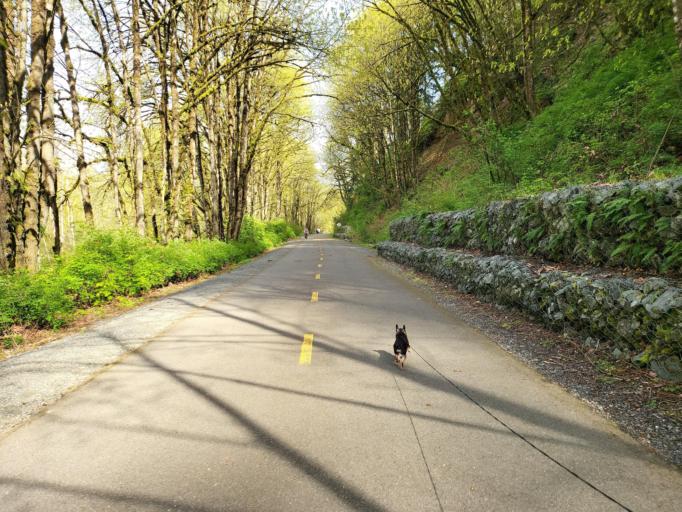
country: US
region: Washington
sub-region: King County
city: Renton
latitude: 47.4757
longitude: -122.1844
